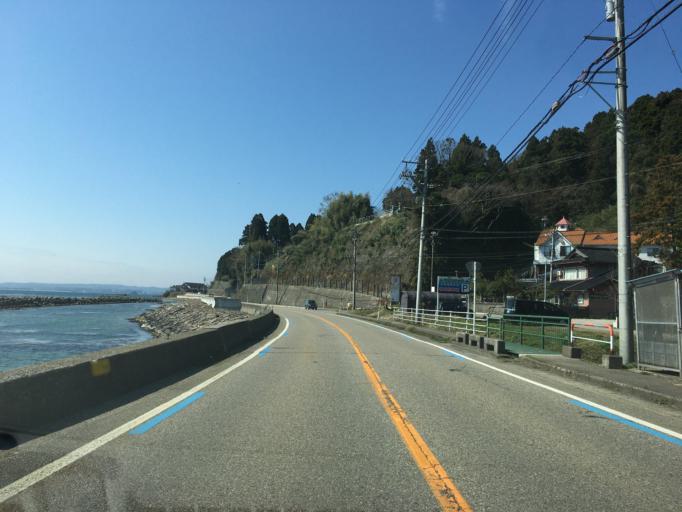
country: JP
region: Toyama
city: Himi
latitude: 36.9038
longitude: 137.0135
